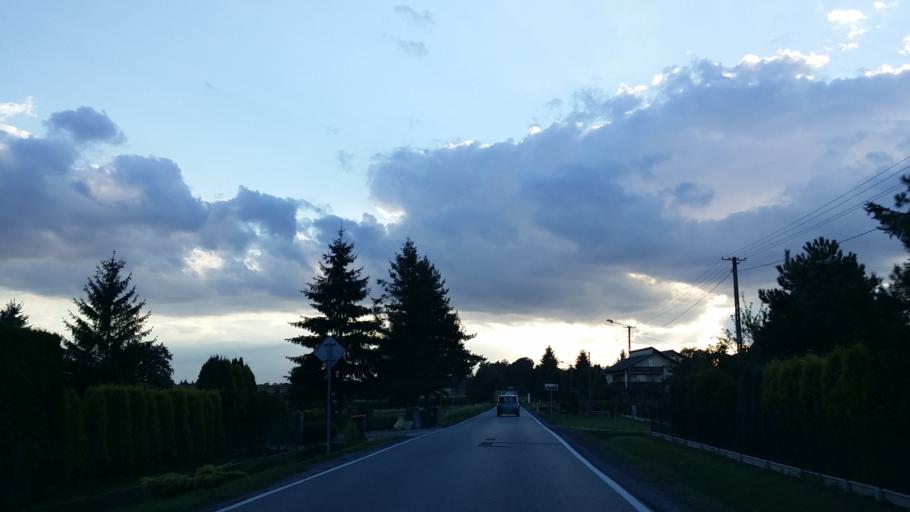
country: PL
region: Lesser Poland Voivodeship
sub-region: Powiat oswiecimski
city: Polanka Wielka
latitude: 49.9898
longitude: 19.3457
